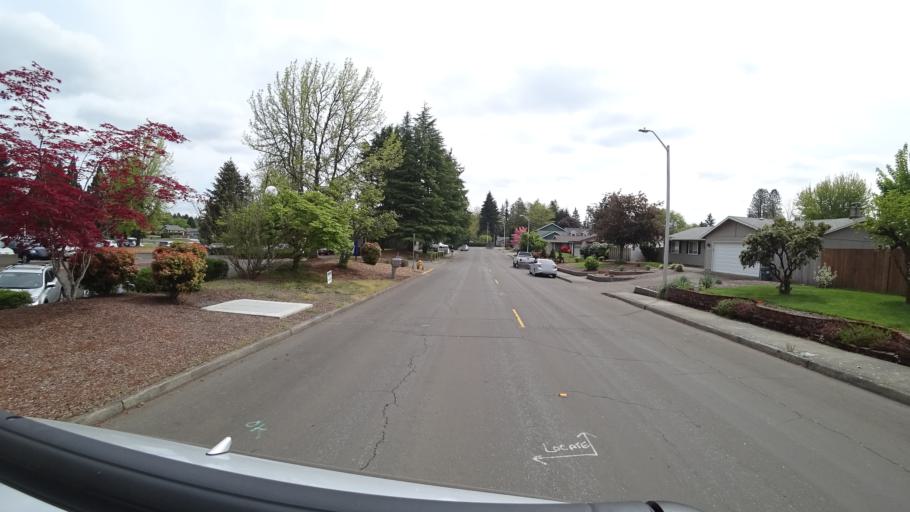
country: US
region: Oregon
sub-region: Washington County
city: Hillsboro
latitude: 45.5299
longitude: -122.9953
